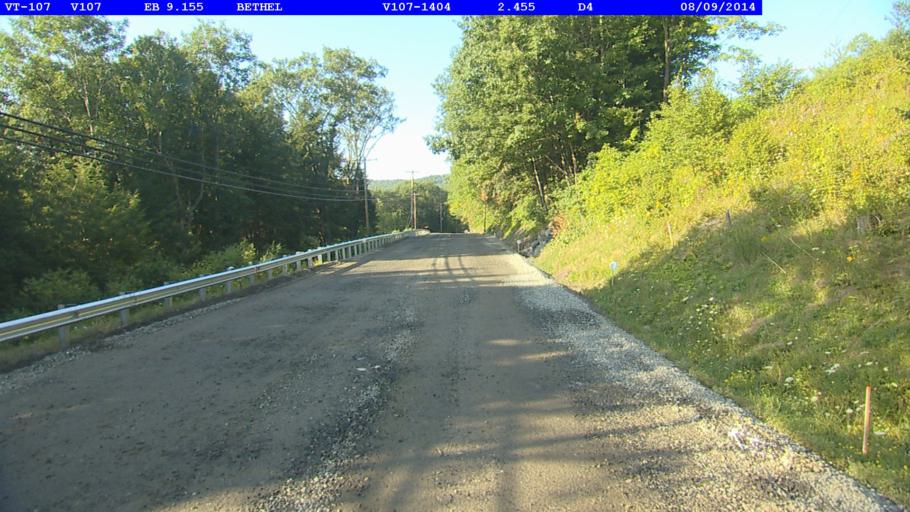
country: US
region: Vermont
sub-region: Orange County
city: Randolph
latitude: 43.8160
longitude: -72.6360
